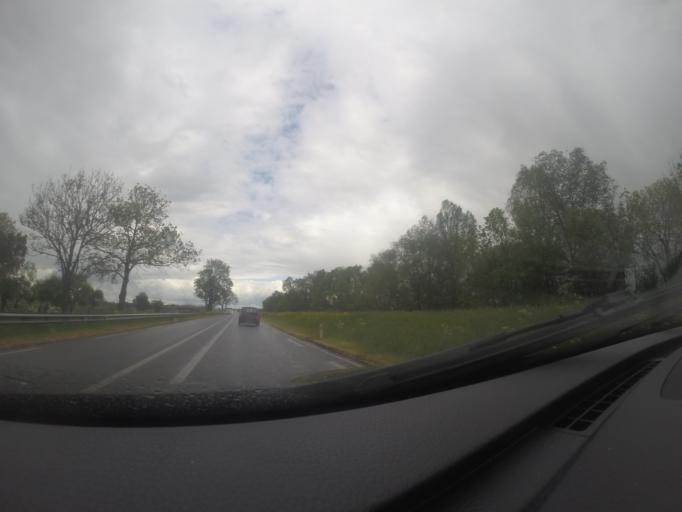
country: NL
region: Gelderland
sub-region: Gemeente Zutphen
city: Zutphen
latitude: 52.1292
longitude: 6.1783
